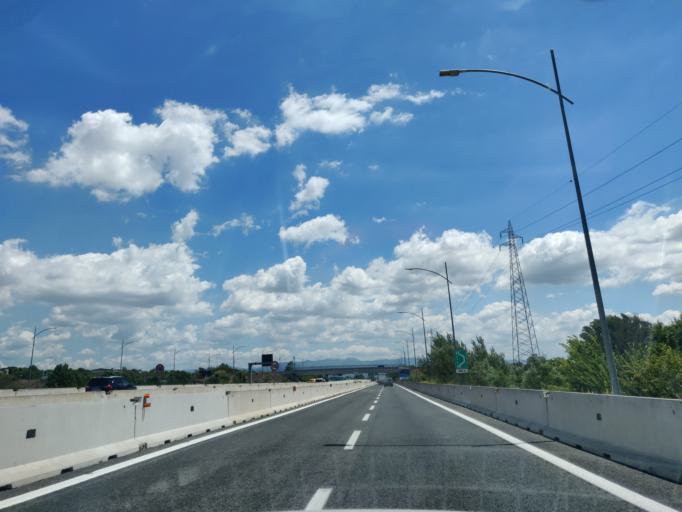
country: IT
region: Latium
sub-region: Citta metropolitana di Roma Capitale
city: Setteville
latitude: 41.9232
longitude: 12.6259
